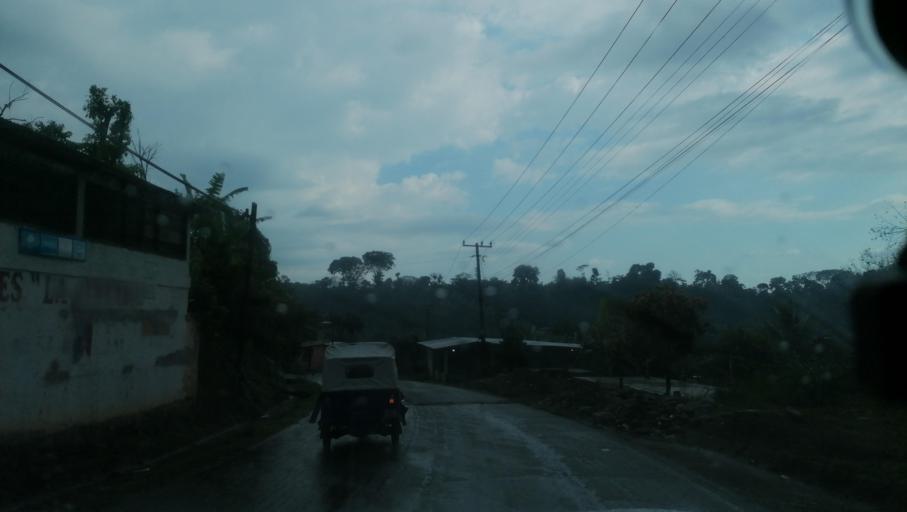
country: MX
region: Chiapas
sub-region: Cacahoatan
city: Benito Juarez
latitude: 15.0522
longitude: -92.1897
